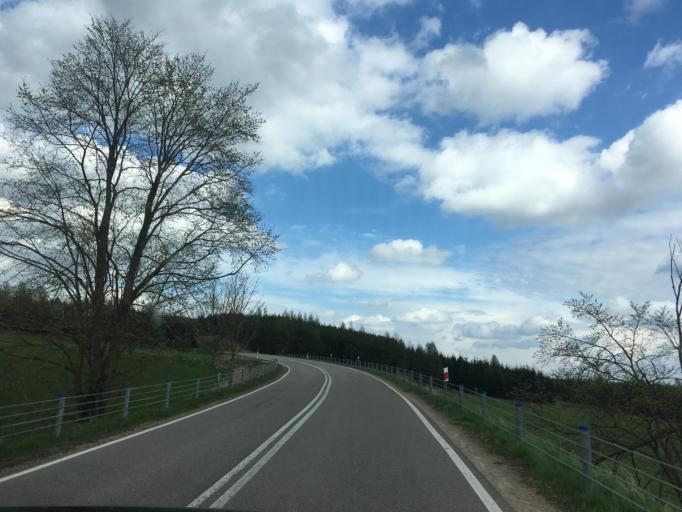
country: PL
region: Podlasie
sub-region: Powiat suwalski
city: Filipow
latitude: 54.3589
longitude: 22.8107
